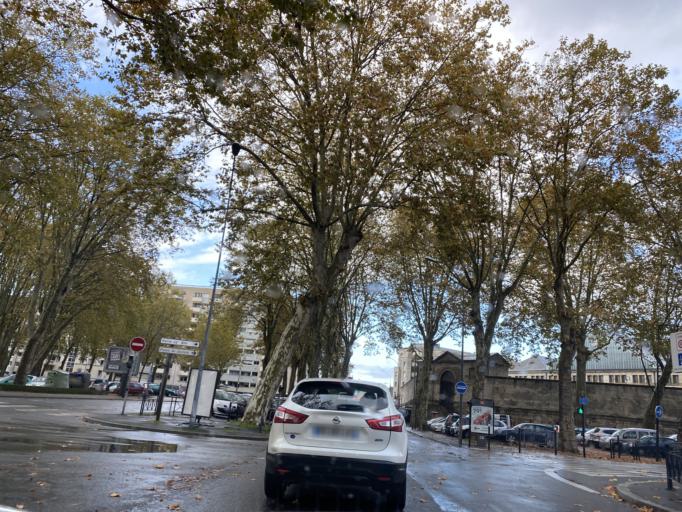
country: FR
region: Centre
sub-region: Departement du Cher
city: Bourges
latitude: 47.0822
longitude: 2.3893
